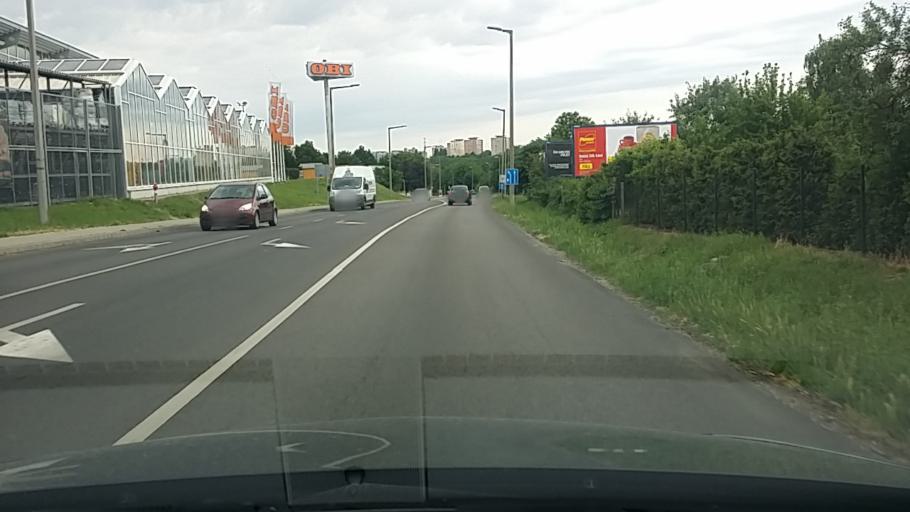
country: HU
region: Fejer
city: dunaujvaros
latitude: 46.9776
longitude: 18.9210
